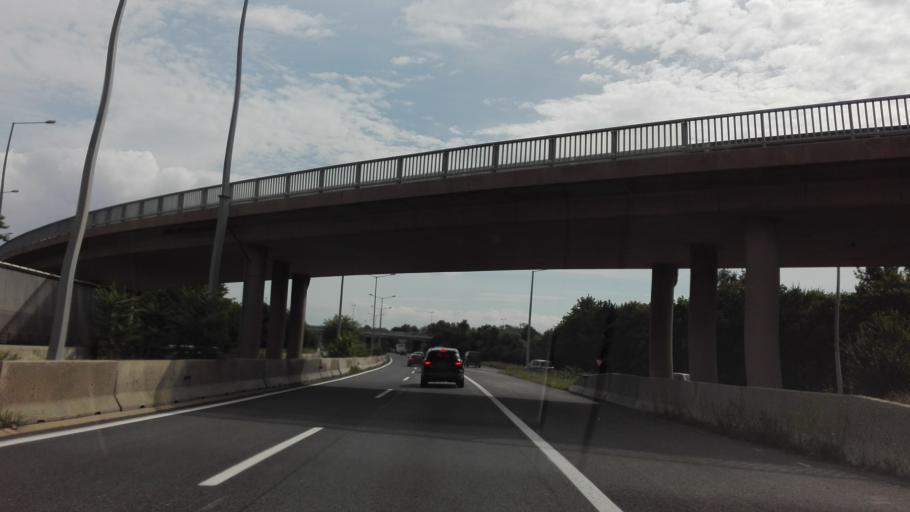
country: AT
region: Lower Austria
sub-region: Politischer Bezirk Modling
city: Brunn am Gebirge
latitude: 48.1161
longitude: 16.2955
